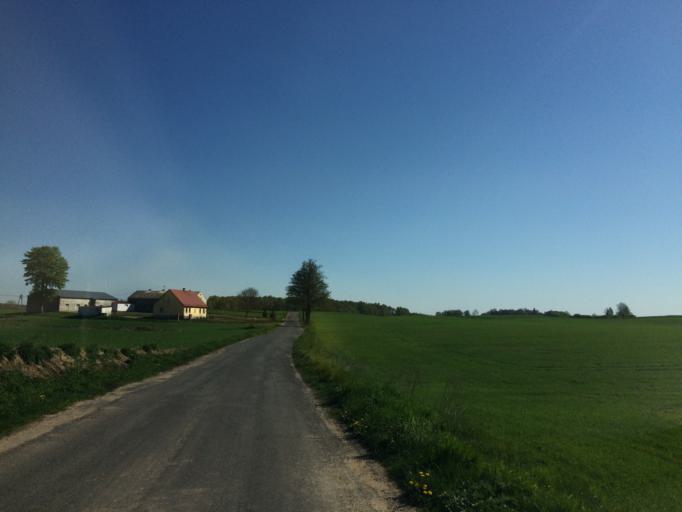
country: PL
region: Warmian-Masurian Voivodeship
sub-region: Powiat dzialdowski
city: Rybno
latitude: 53.4520
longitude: 19.9298
